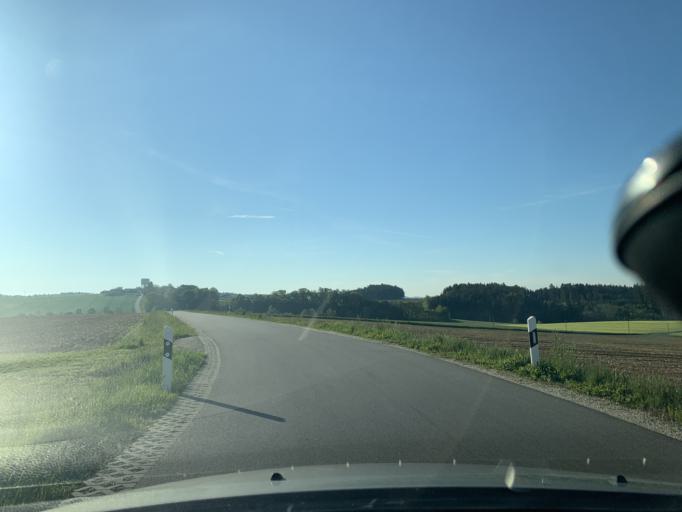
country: DE
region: Bavaria
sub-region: Lower Bavaria
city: Adlkofen
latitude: 48.5210
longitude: 12.3080
